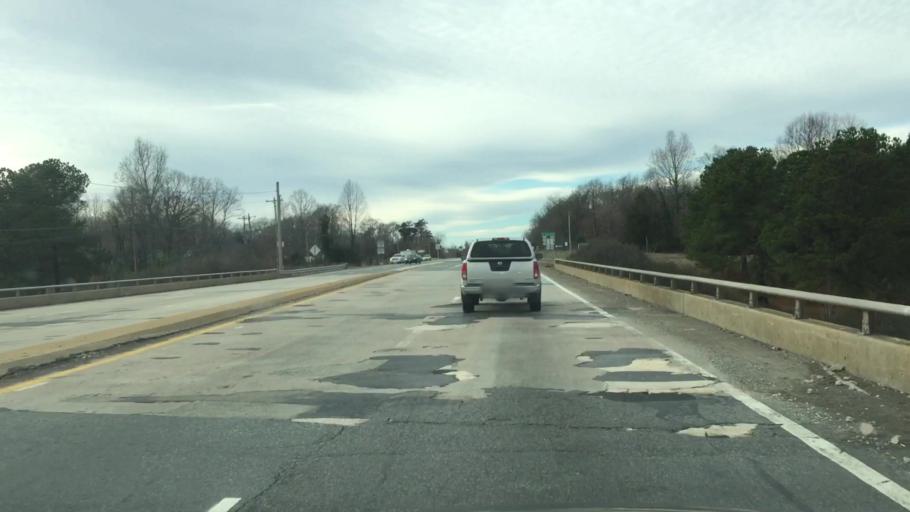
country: US
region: North Carolina
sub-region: Rockingham County
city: Reidsville
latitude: 36.3603
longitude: -79.6270
